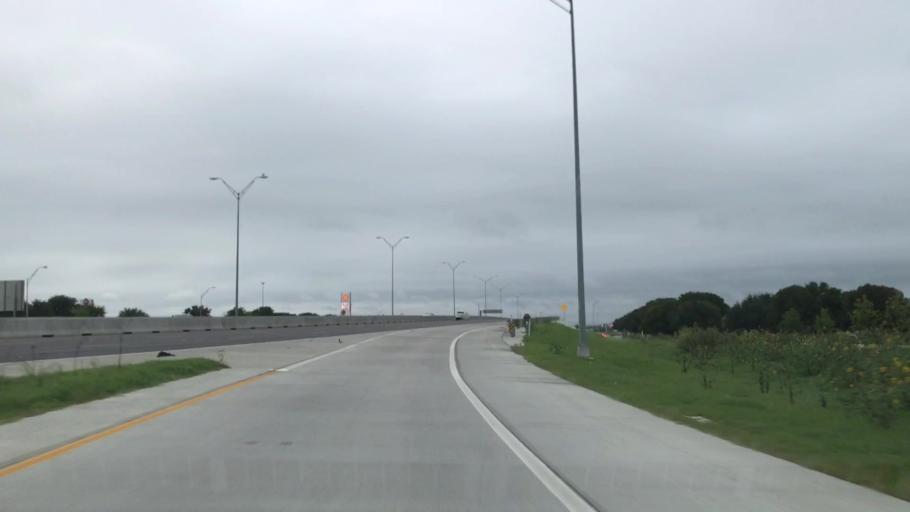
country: US
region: Texas
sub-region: Dallas County
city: Coppell
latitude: 32.9198
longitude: -97.0166
